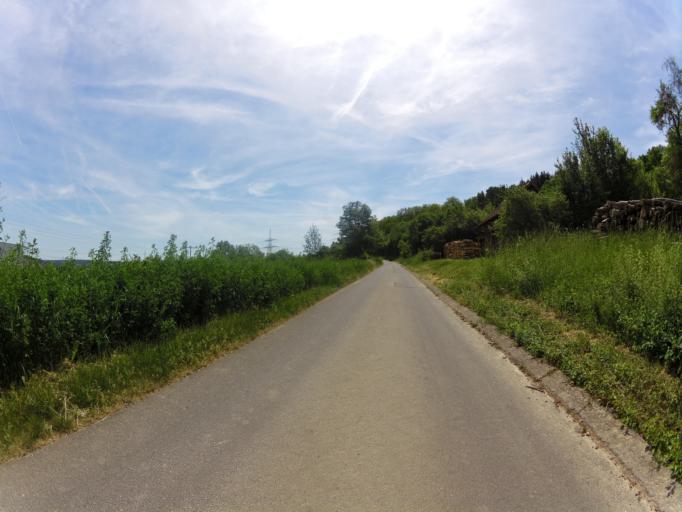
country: DE
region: Bavaria
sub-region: Regierungsbezirk Unterfranken
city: Sommerhausen
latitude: 49.6757
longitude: 10.0307
